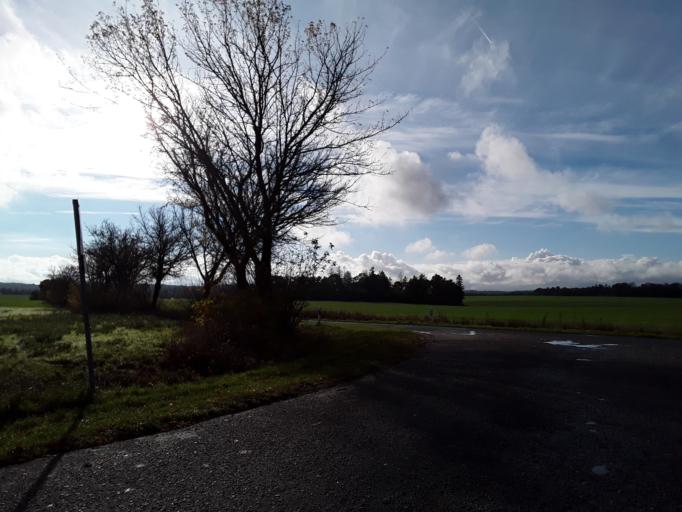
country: DE
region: Brandenburg
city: Mittenwalde
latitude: 53.2818
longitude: 13.7073
